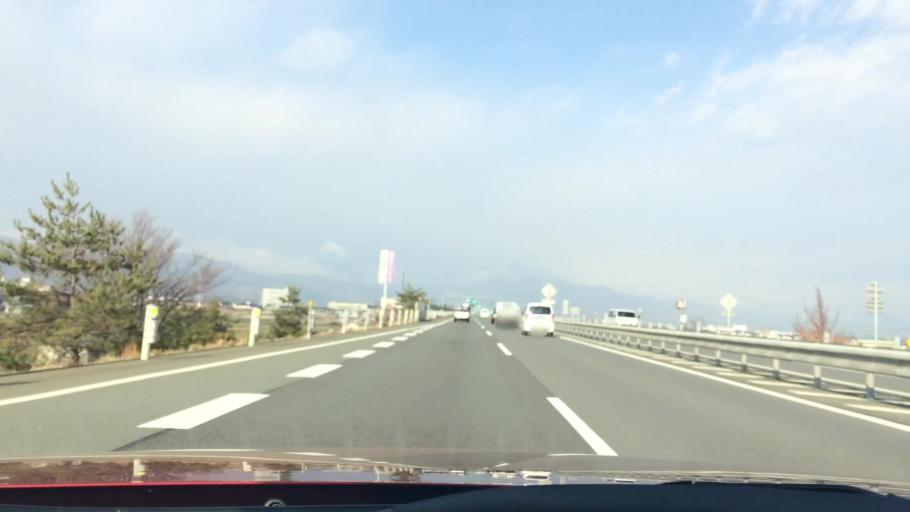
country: JP
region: Nagano
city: Nagano-shi
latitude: 36.5374
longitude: 138.1399
